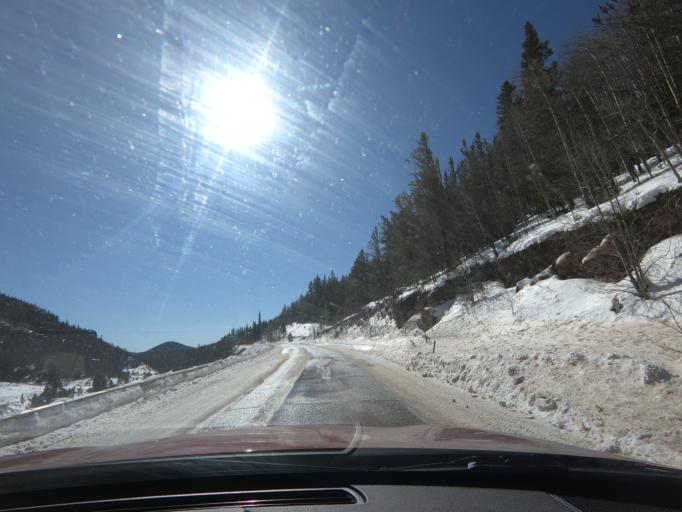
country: US
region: Colorado
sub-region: Teller County
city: Cripple Creek
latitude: 38.7529
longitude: -105.1030
